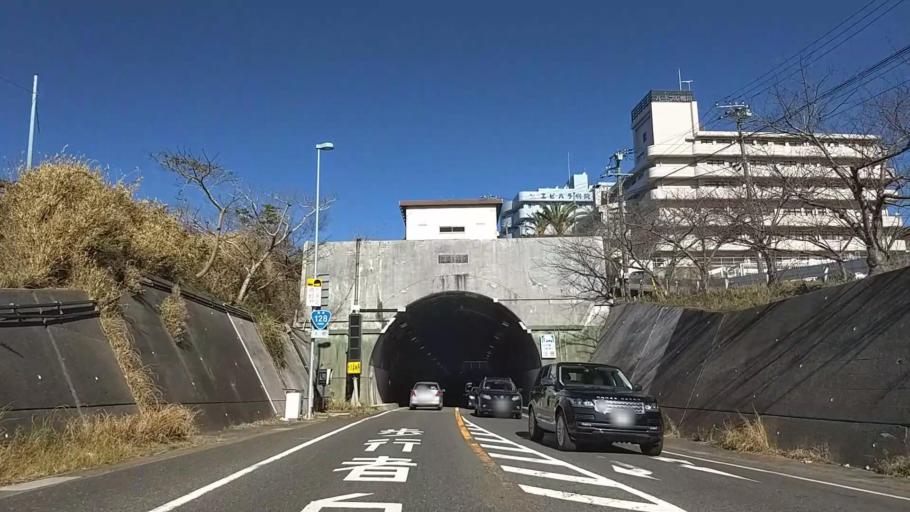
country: JP
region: Chiba
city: Kawaguchi
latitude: 35.0901
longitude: 140.0902
